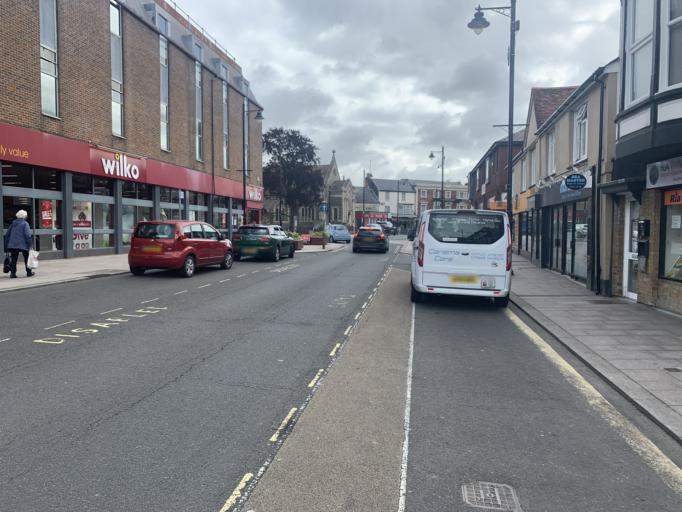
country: GB
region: England
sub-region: Hampshire
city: Andover
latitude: 51.2060
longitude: -1.4817
